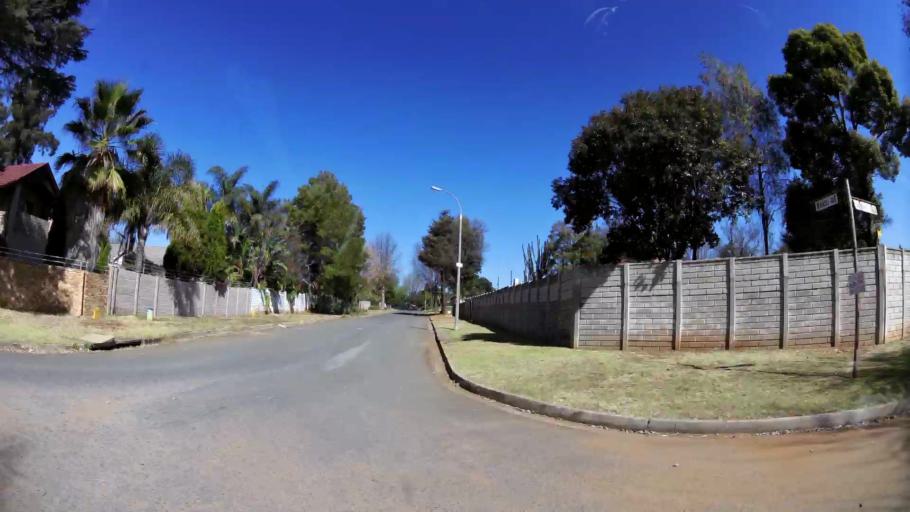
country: ZA
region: Gauteng
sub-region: City of Johannesburg Metropolitan Municipality
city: Modderfontein
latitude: -26.0616
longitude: 28.2123
